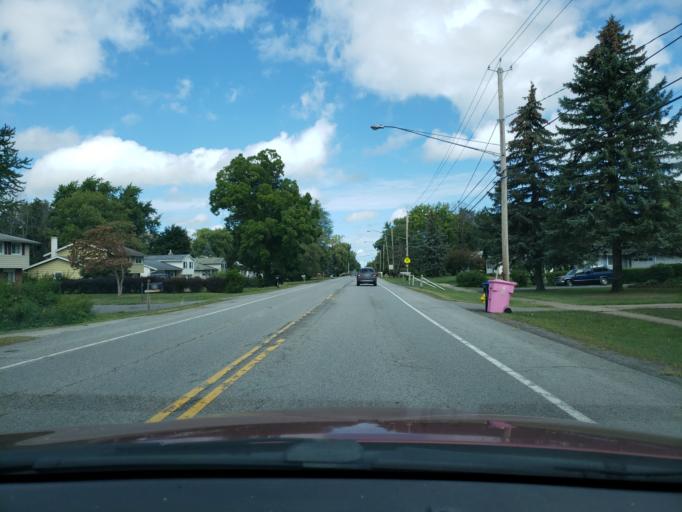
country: US
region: New York
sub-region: Monroe County
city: Greece
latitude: 43.2209
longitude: -77.7338
